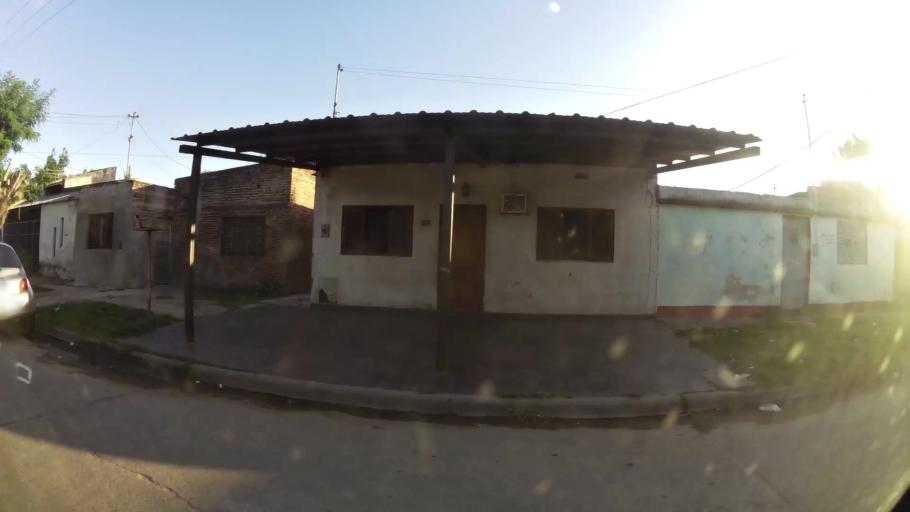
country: AR
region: Santa Fe
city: Santa Fe de la Vera Cruz
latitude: -31.5996
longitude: -60.6817
